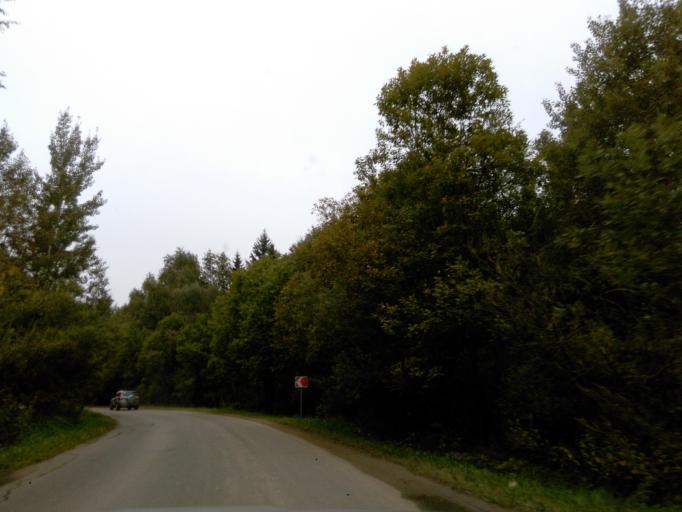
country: RU
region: Moskovskaya
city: Mendeleyevo
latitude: 56.1022
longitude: 37.2698
